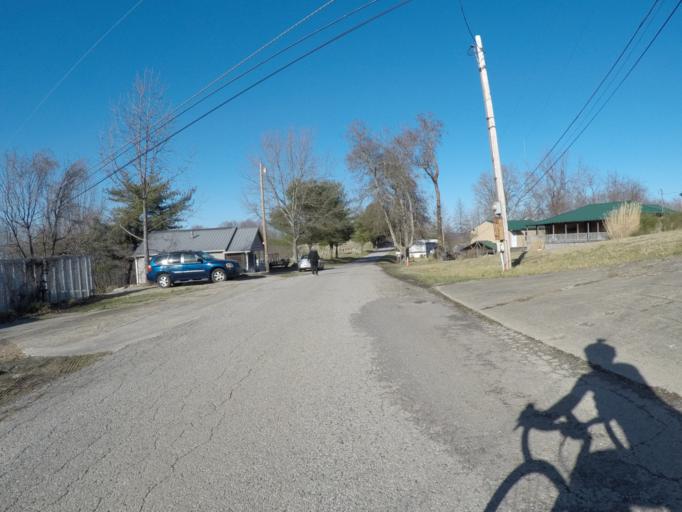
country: US
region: West Virginia
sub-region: Wayne County
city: Ceredo
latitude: 38.3861
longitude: -82.5643
